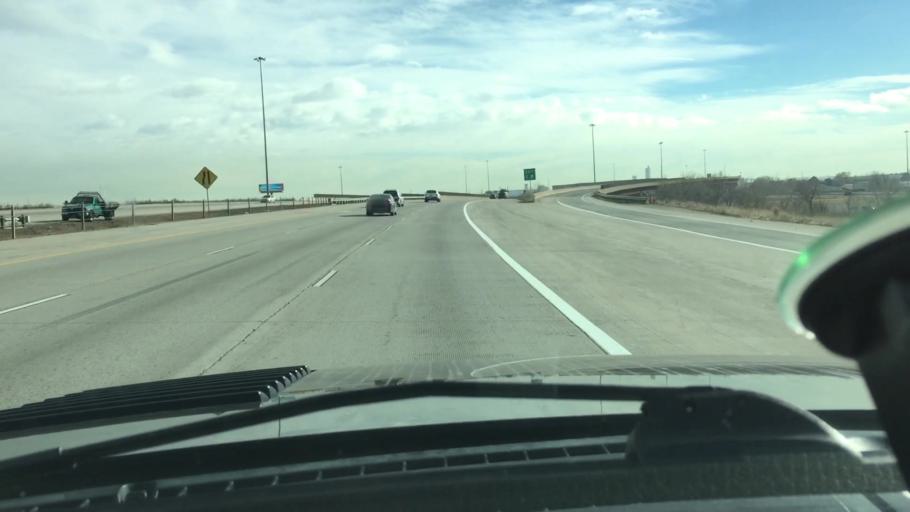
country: US
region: Colorado
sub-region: Adams County
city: Welby
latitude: 39.8268
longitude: -104.9717
